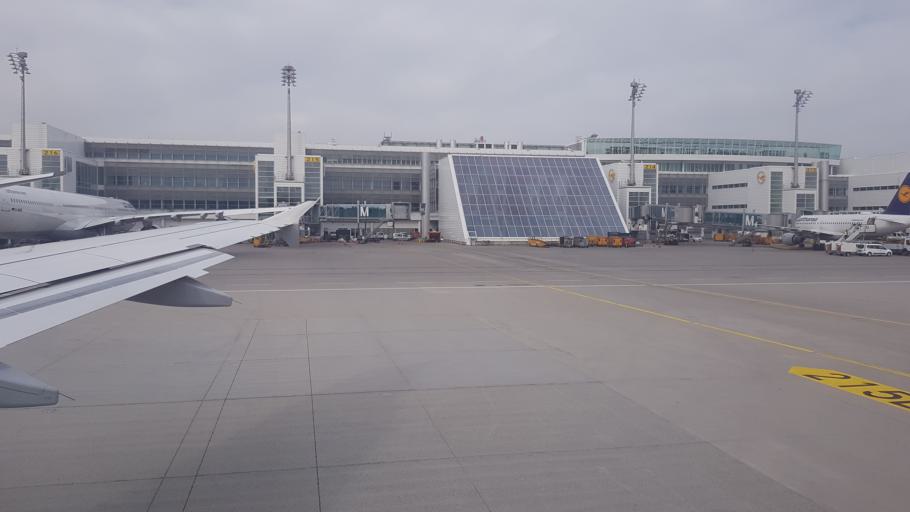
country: DE
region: Bavaria
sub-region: Upper Bavaria
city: Hallbergmoos
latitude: 48.3528
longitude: 11.7951
